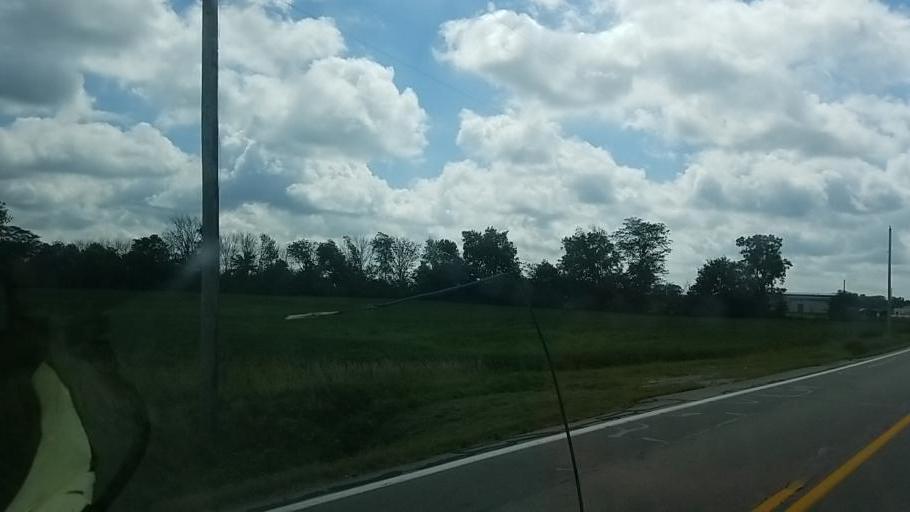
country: US
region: Ohio
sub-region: Madison County
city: Bethel
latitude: 39.7014
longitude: -83.4597
